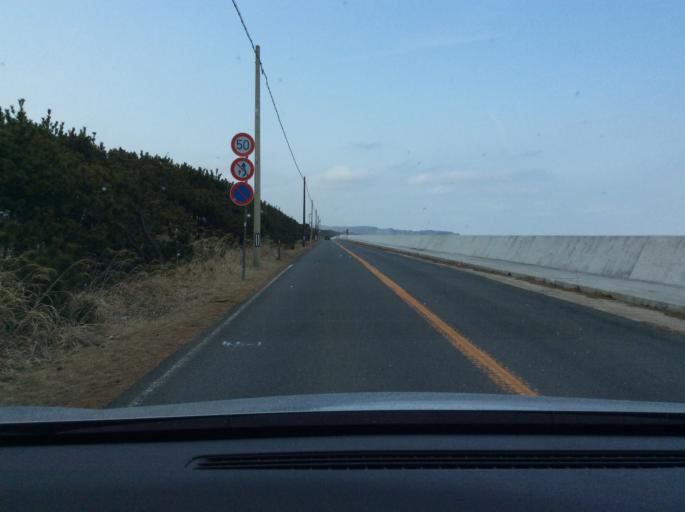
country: JP
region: Fukushima
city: Iwaki
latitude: 37.0628
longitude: 140.9754
